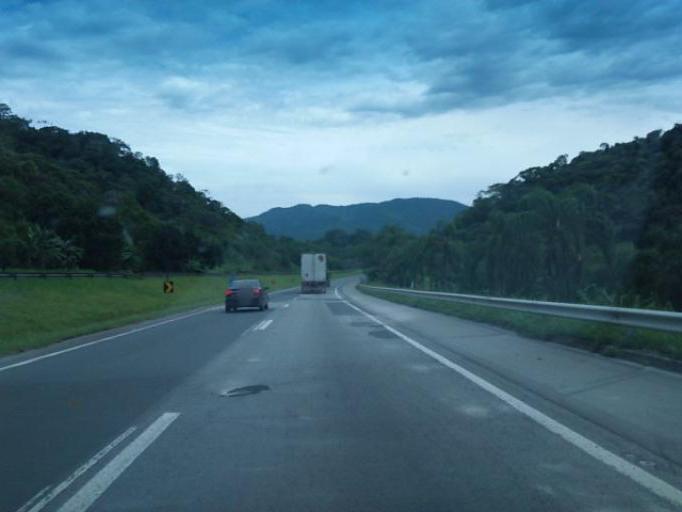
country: BR
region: Sao Paulo
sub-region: Miracatu
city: Miracatu
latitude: -24.2342
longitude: -47.3606
